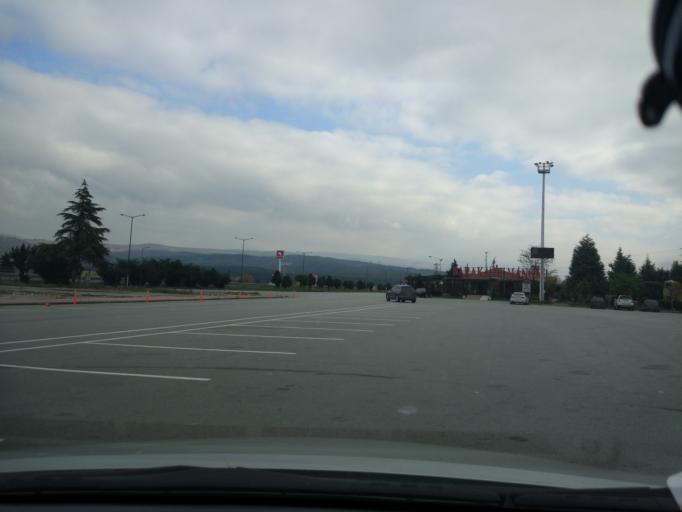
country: TR
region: Duzce
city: Kaynasli
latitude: 40.7898
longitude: 31.2407
